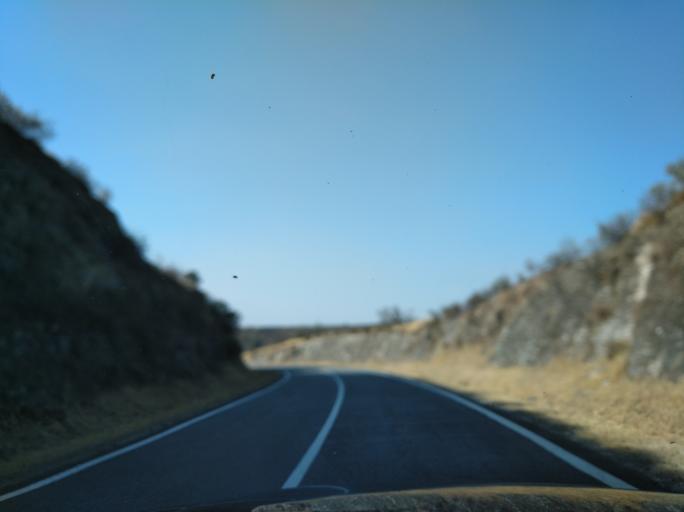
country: ES
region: Extremadura
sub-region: Provincia de Badajoz
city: Valencia del Mombuey
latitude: 38.1470
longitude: -7.2365
